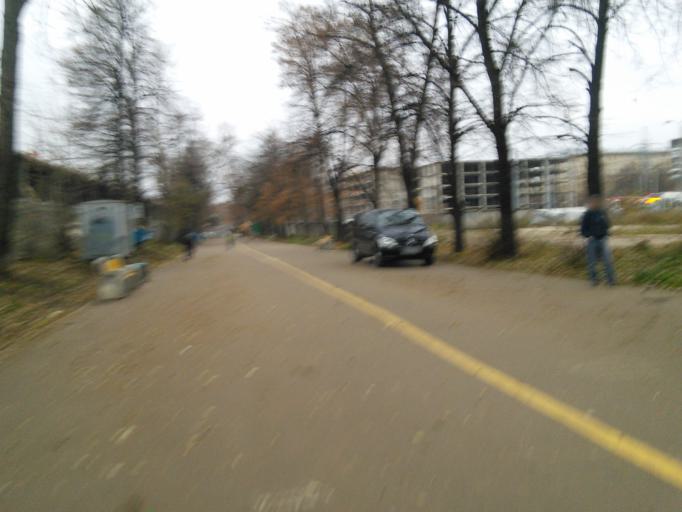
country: RU
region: Moscow
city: Mar'ina Roshcha
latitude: 55.8082
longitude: 37.5790
